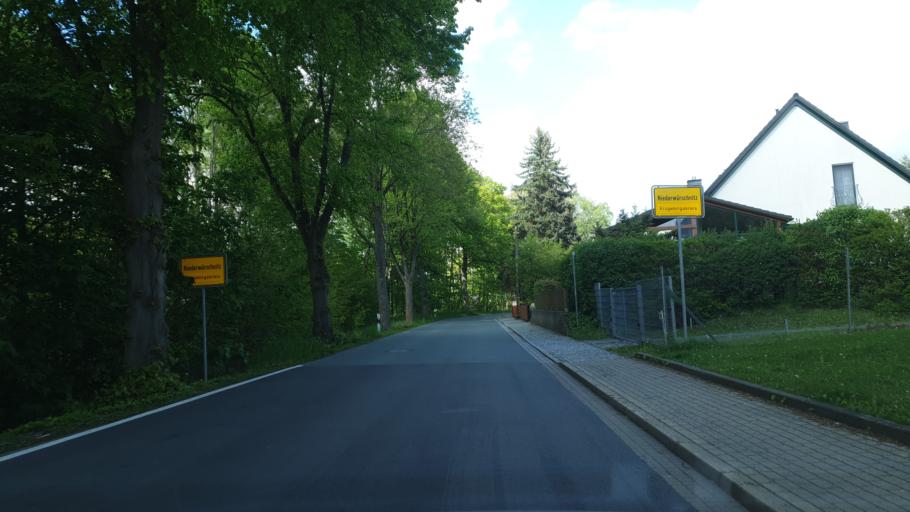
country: DE
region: Saxony
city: Lugau
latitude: 50.7180
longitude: 12.7445
